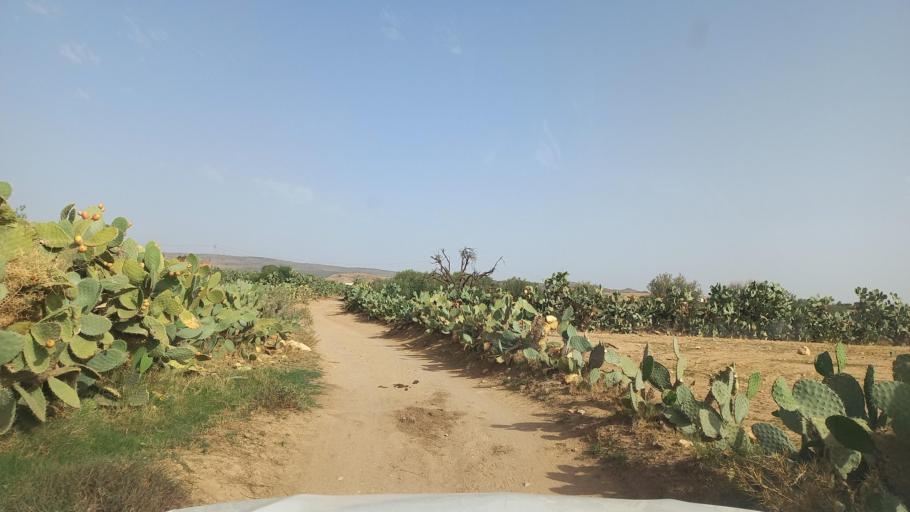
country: TN
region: Al Qasrayn
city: Kasserine
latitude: 35.2981
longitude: 8.9630
